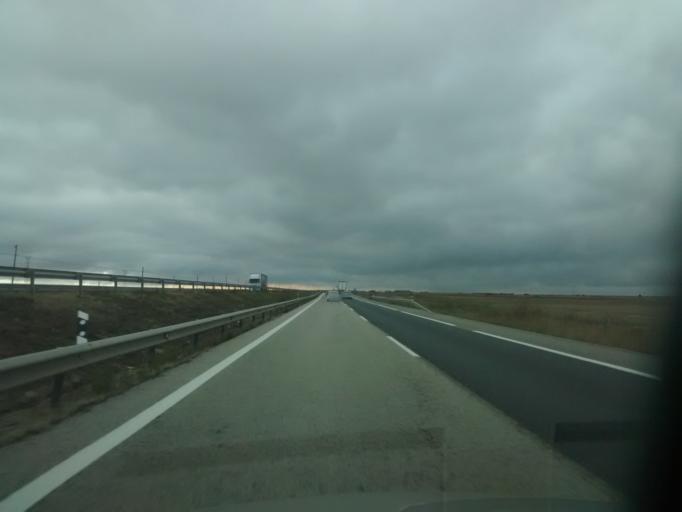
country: ES
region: Castille-La Mancha
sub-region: Provincia de Guadalajara
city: Almadrones
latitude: 40.8833
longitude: -2.7857
